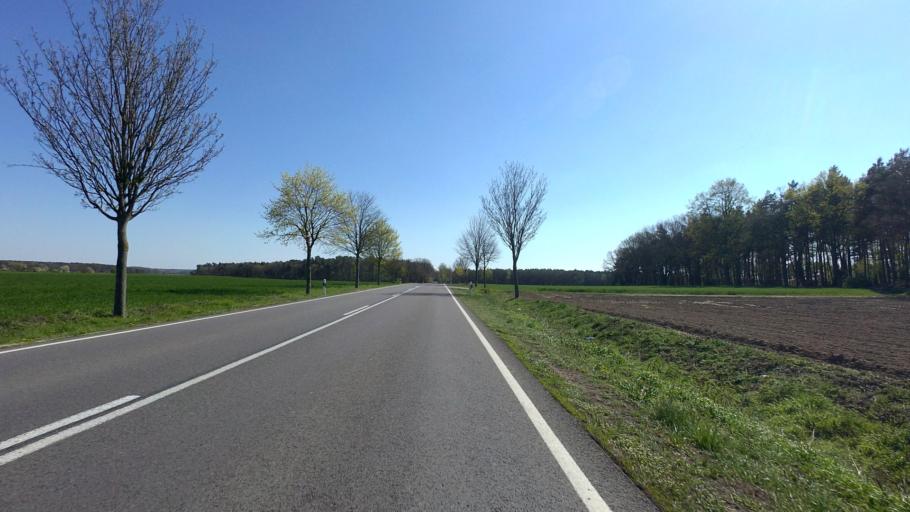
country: DE
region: Saxony-Anhalt
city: Pretzier
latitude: 52.7121
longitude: 11.2509
